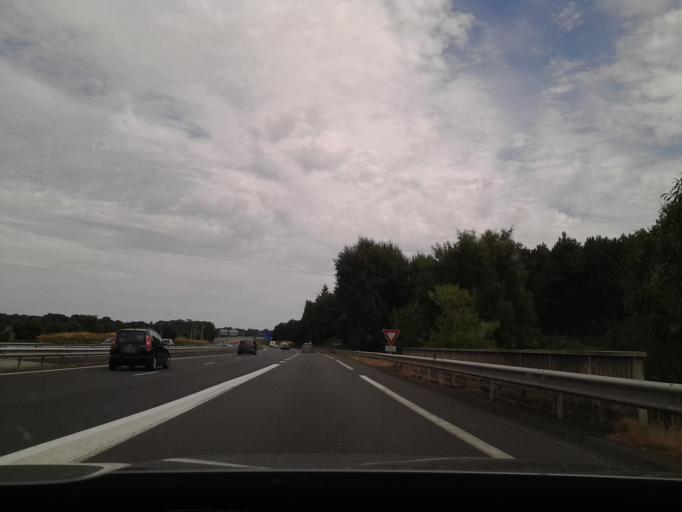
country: FR
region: Pays de la Loire
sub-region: Departement de la Sarthe
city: Rouillon
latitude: 48.0224
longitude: 0.1315
